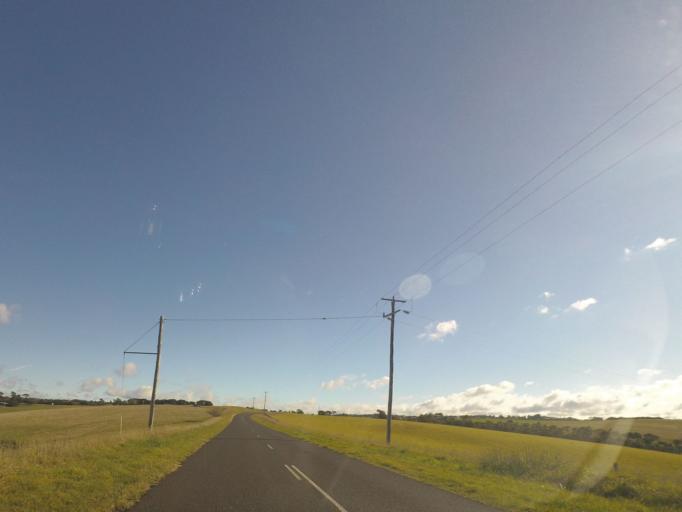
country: AU
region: Victoria
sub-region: Moorabool
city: Bacchus Marsh
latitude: -37.6385
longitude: 144.3611
